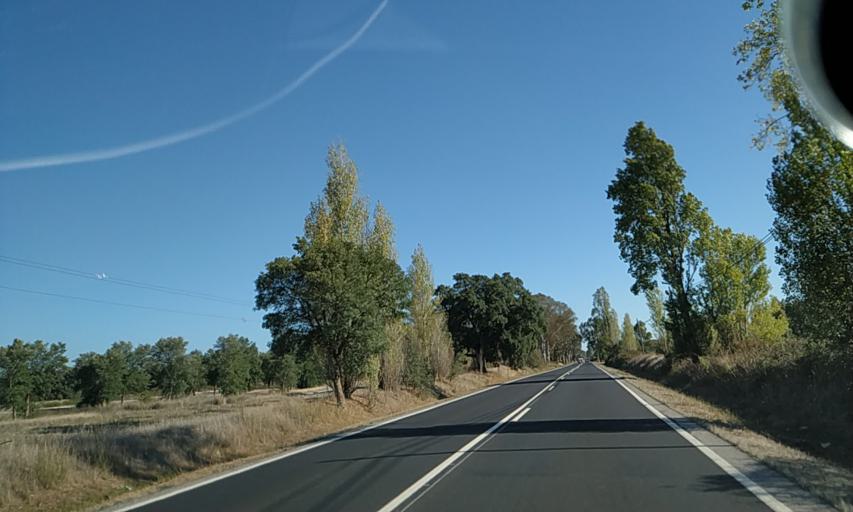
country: PT
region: Santarem
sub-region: Benavente
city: Poceirao
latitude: 38.8053
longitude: -8.8808
